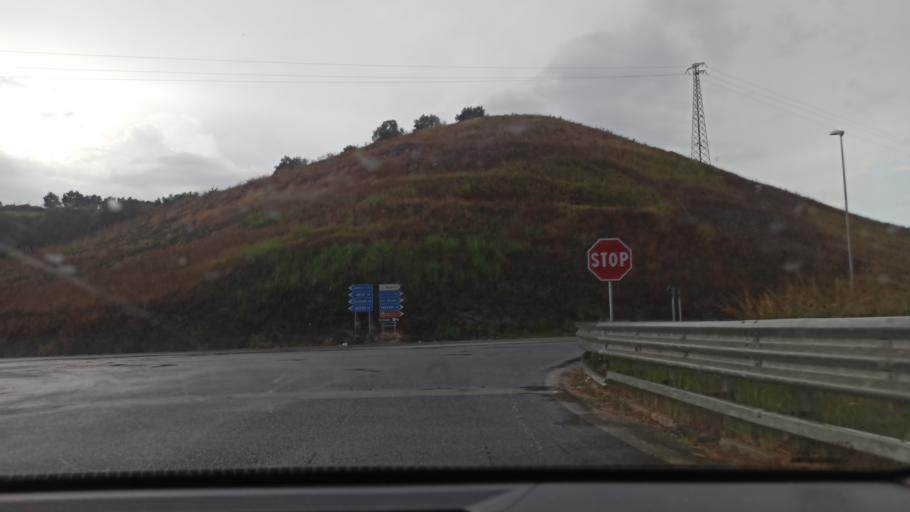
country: IT
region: Calabria
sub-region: Provincia di Vibo-Valentia
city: Paravati
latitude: 38.5657
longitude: 16.0808
